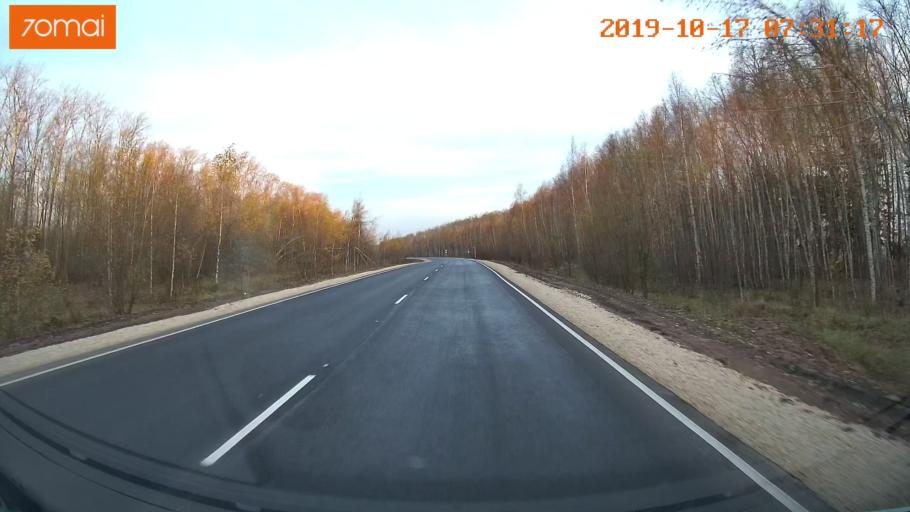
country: RU
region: Ivanovo
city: Gavrilov Posad
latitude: 56.3873
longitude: 39.9990
